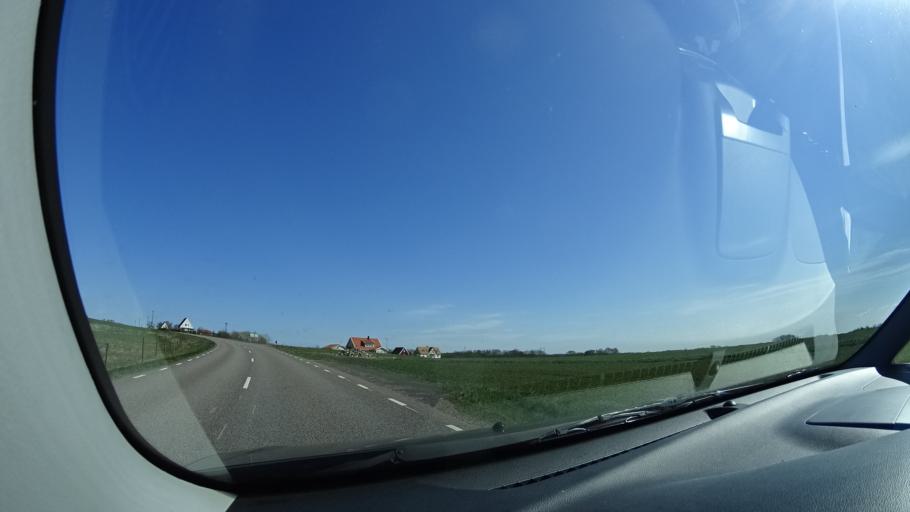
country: SE
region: Skane
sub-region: Hoganas Kommun
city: Hoganas
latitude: 56.2511
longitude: 12.5682
